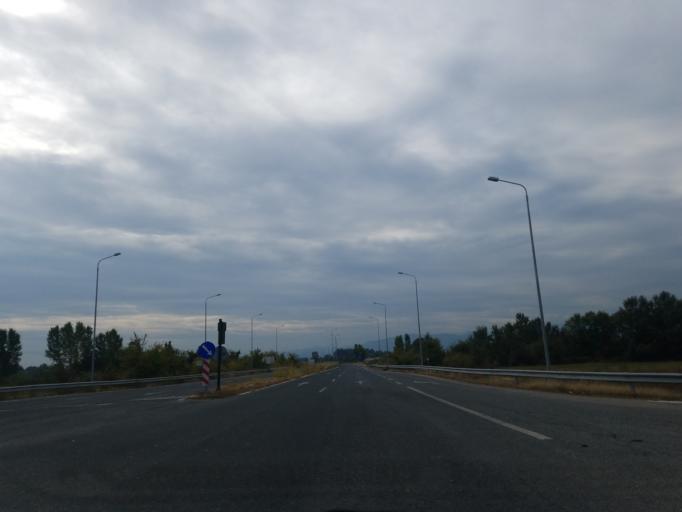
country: GR
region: Thessaly
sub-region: Trikala
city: Pyrgetos
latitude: 39.5411
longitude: 21.7356
